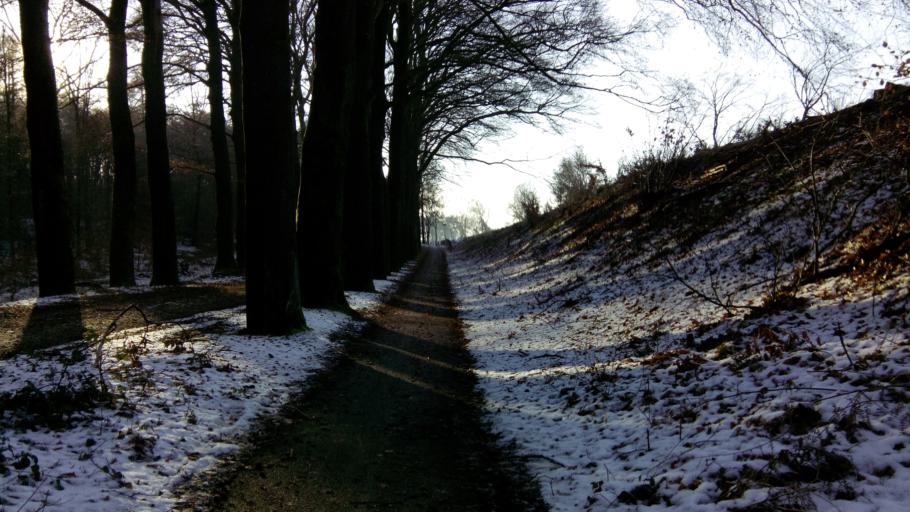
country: NL
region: Gelderland
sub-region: Gemeente Groesbeek
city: Berg en Dal
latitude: 51.7867
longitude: 5.8874
